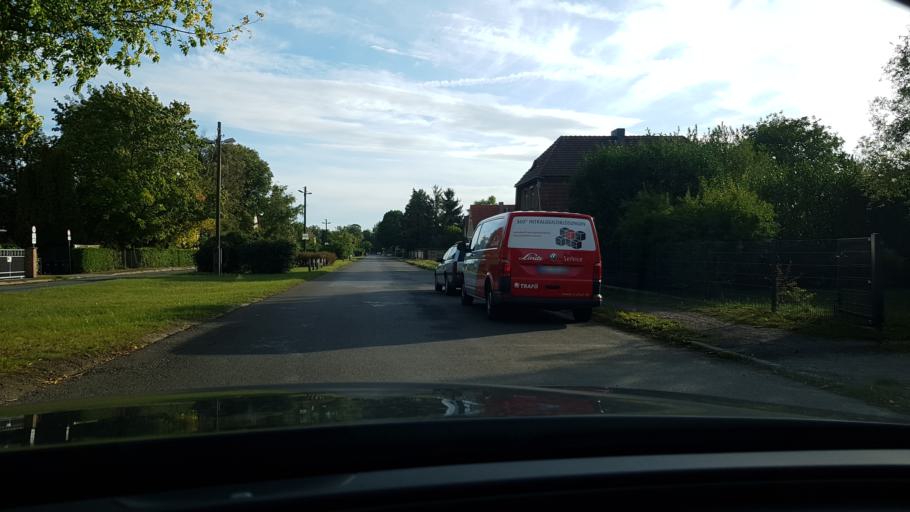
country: DE
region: Brandenburg
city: Brieselang
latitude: 52.5860
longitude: 13.0040
